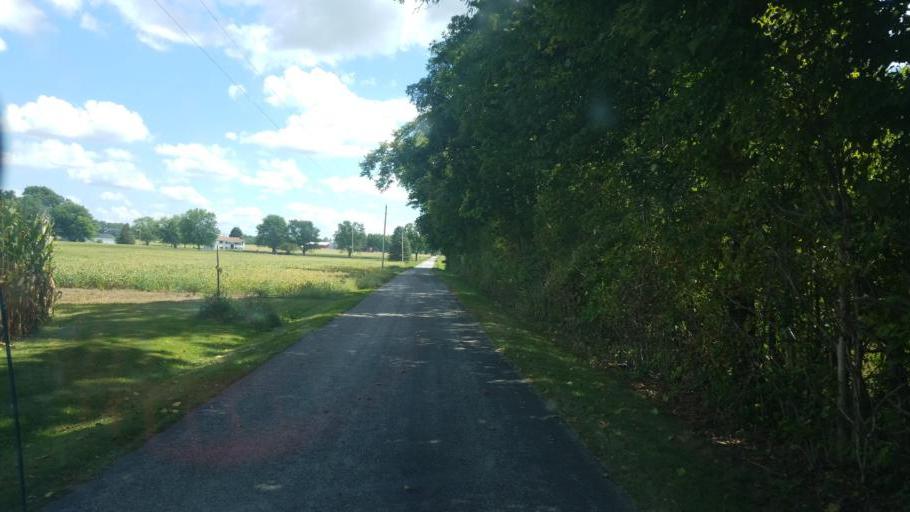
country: US
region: Ohio
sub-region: Marion County
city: Prospect
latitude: 40.4138
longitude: -83.1959
